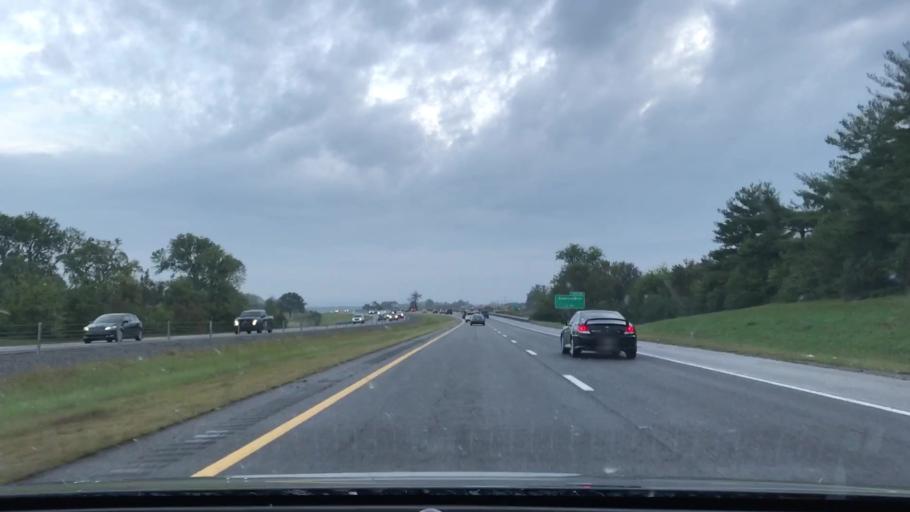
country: US
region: Tennessee
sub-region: Sumner County
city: Gallatin
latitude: 36.3699
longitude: -86.5124
